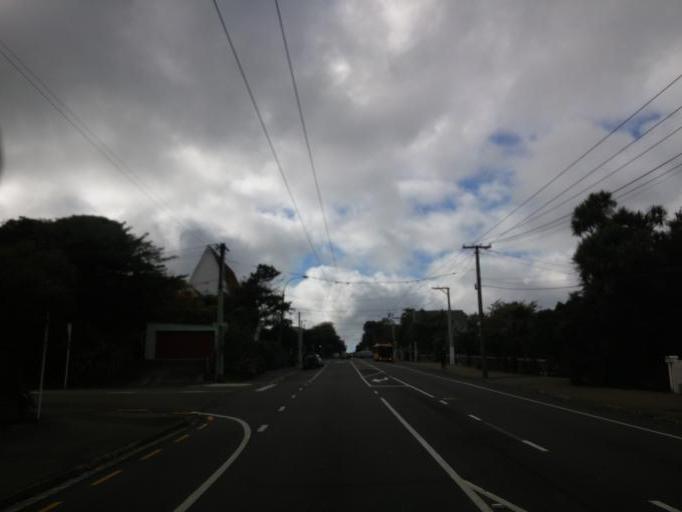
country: NZ
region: Wellington
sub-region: Wellington City
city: Kelburn
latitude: -41.2839
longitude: 174.7399
